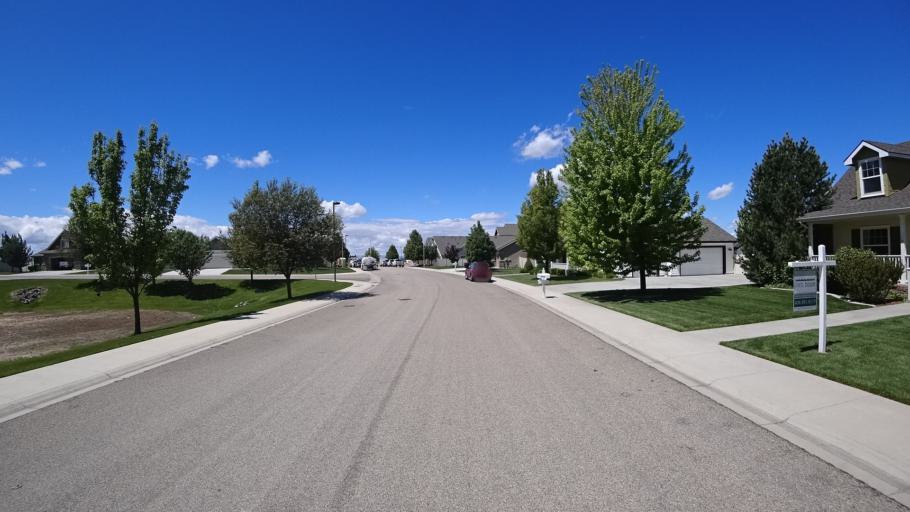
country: US
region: Idaho
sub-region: Ada County
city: Kuna
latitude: 43.5132
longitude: -116.4315
